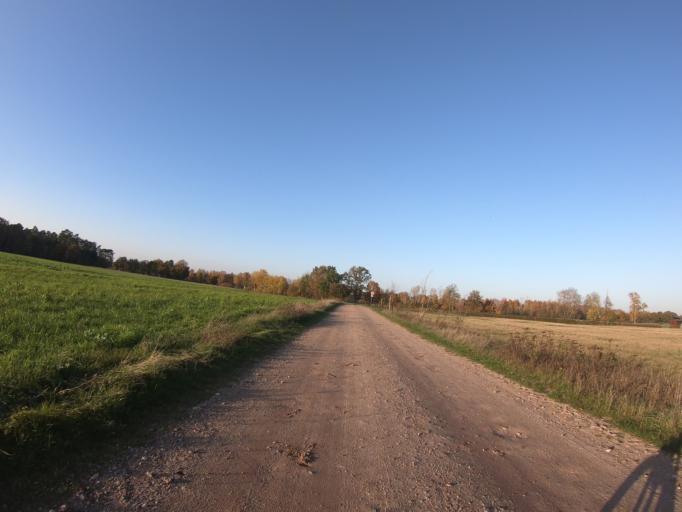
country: DE
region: Lower Saxony
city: Wagenhoff
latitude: 52.5096
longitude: 10.5120
